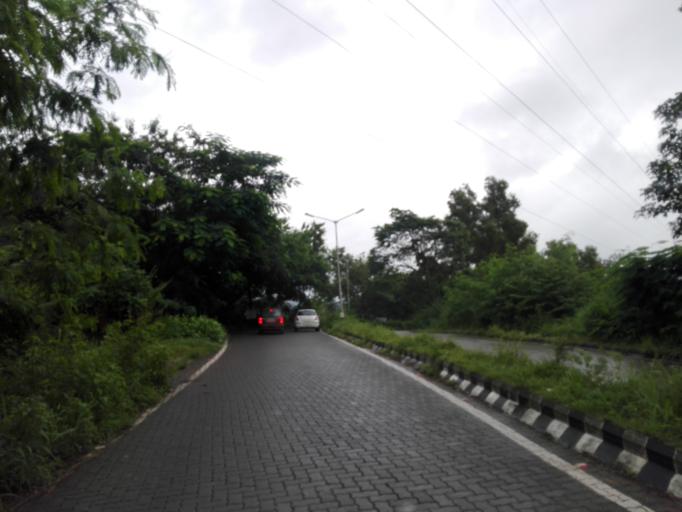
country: IN
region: Kerala
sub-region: Ernakulam
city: Aluva
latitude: 10.0559
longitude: 76.3563
